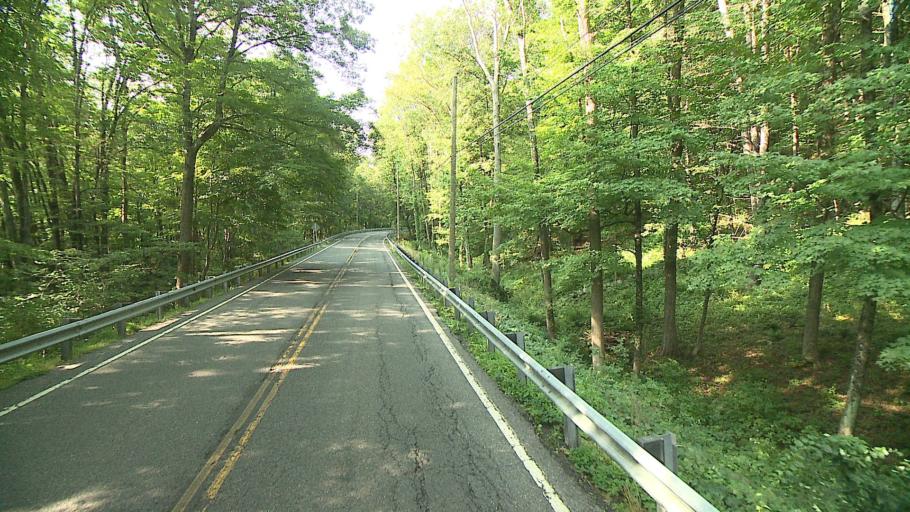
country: US
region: Connecticut
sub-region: Litchfield County
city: Canaan
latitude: 41.8877
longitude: -73.3621
